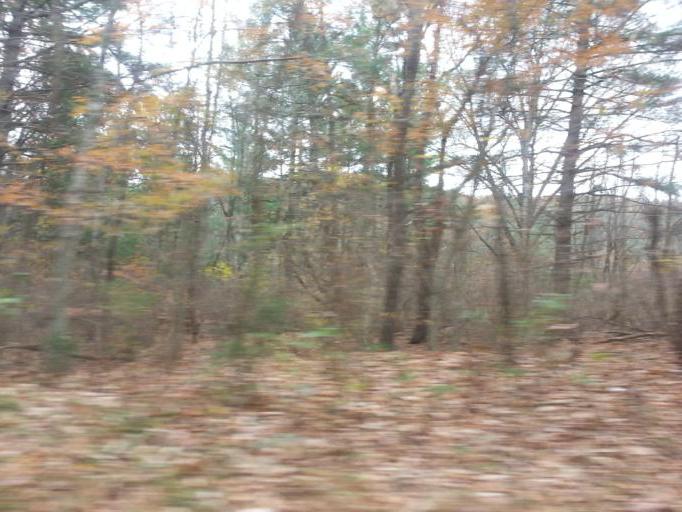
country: US
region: Virginia
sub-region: Pulaski County
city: Pulaski
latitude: 37.1074
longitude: -80.8917
